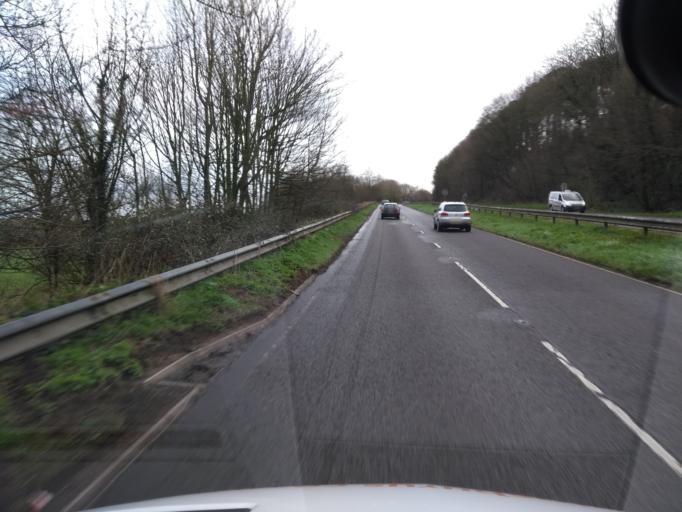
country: GB
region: England
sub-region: Somerset
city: Yeovil
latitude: 50.9410
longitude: -2.6006
